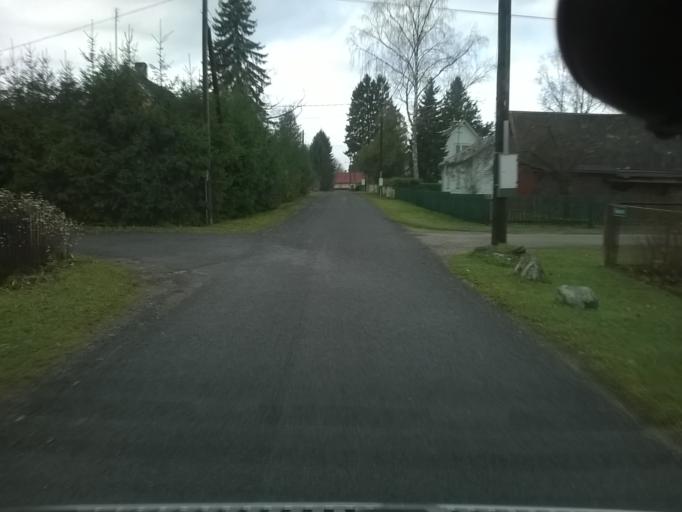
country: EE
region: Laeaene
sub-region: Ridala Parish
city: Uuemoisa
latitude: 58.9505
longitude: 23.7289
